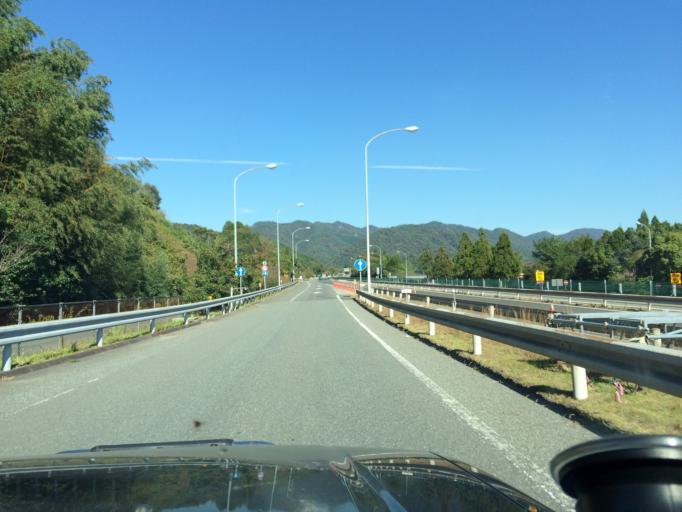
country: JP
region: Hyogo
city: Sasayama
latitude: 35.0923
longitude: 135.1675
